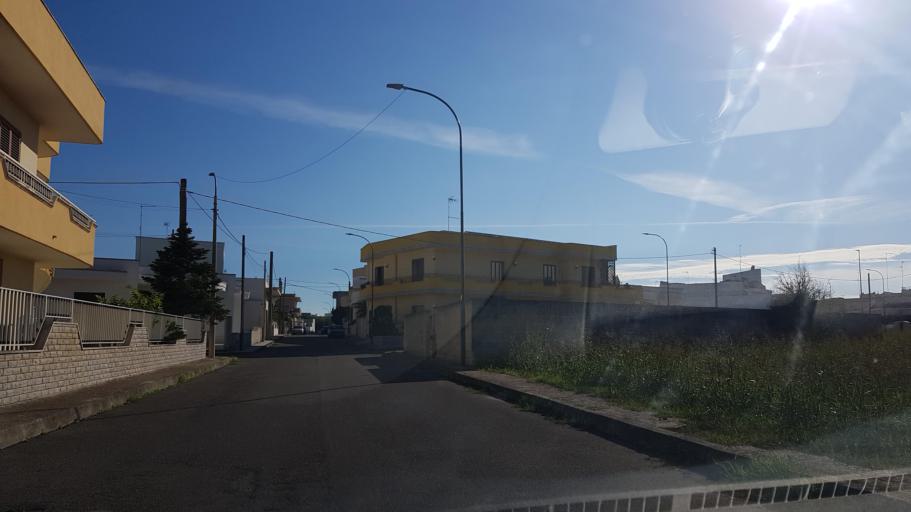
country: IT
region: Apulia
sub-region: Provincia di Lecce
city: Salice Salentino
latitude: 40.3896
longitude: 17.9612
